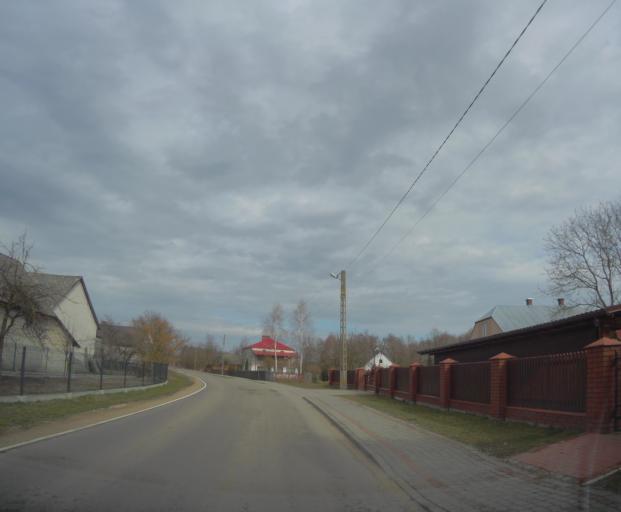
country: PL
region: Subcarpathian Voivodeship
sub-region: Powiat nizanski
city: Ulanow
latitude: 50.5066
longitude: 22.3075
